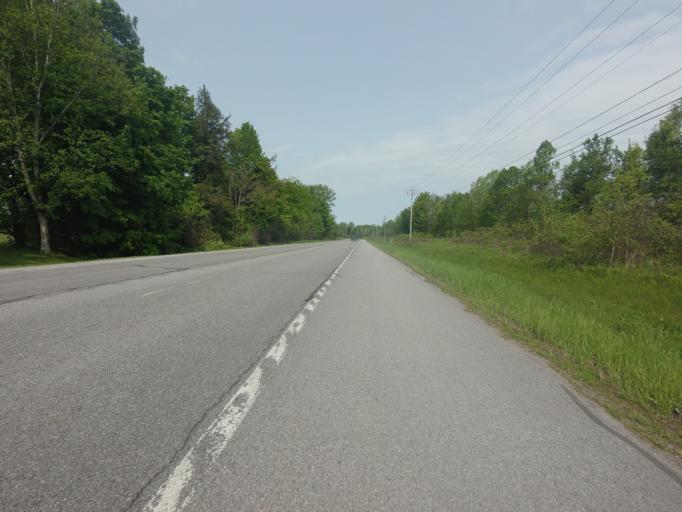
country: US
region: New York
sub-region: Jefferson County
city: Brownville
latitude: 44.0073
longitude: -76.0113
